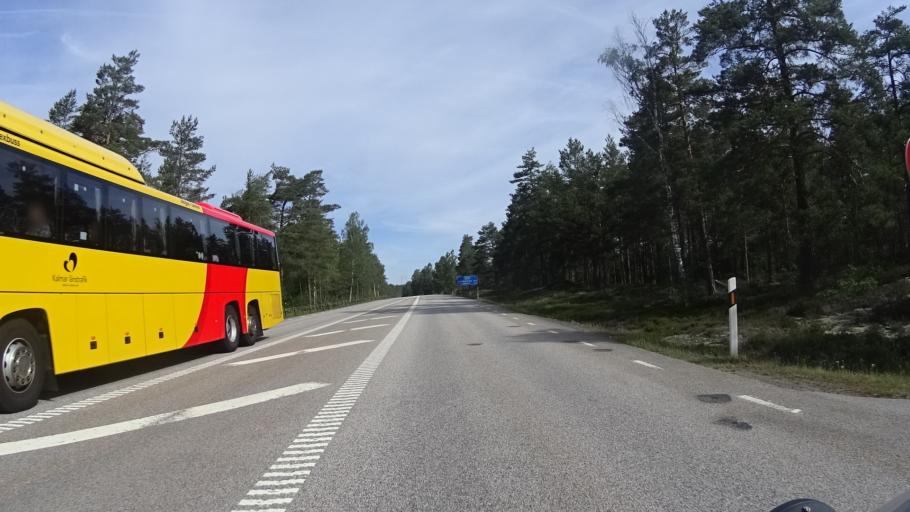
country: SE
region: Kalmar
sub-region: Vasterviks Kommun
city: Ankarsrum
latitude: 57.5251
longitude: 16.4923
